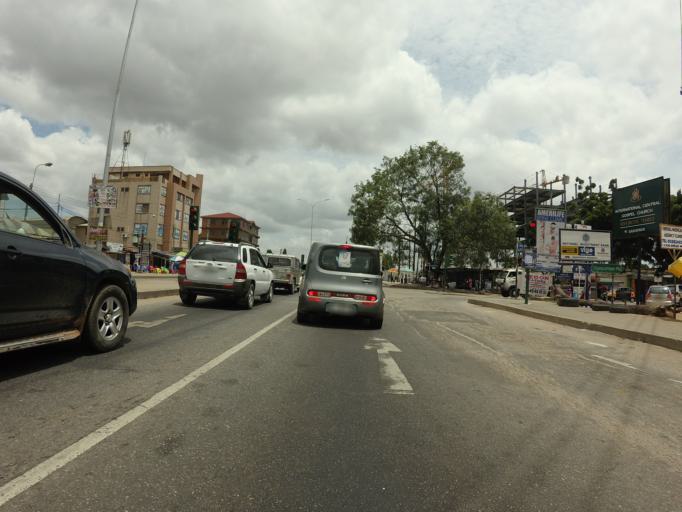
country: GH
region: Greater Accra
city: Gbawe
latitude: 5.5759
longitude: -0.2750
